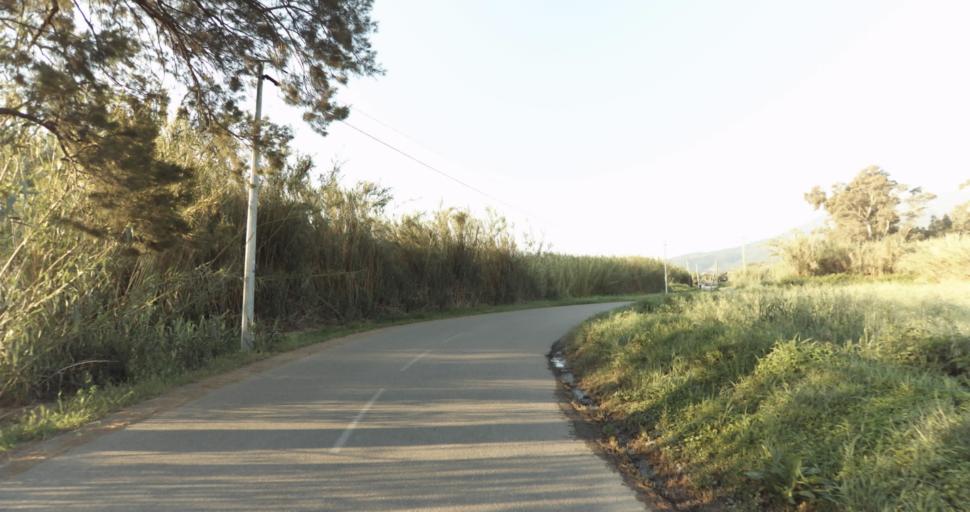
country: FR
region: Corsica
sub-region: Departement de la Haute-Corse
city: Biguglia
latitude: 42.6141
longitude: 9.4441
